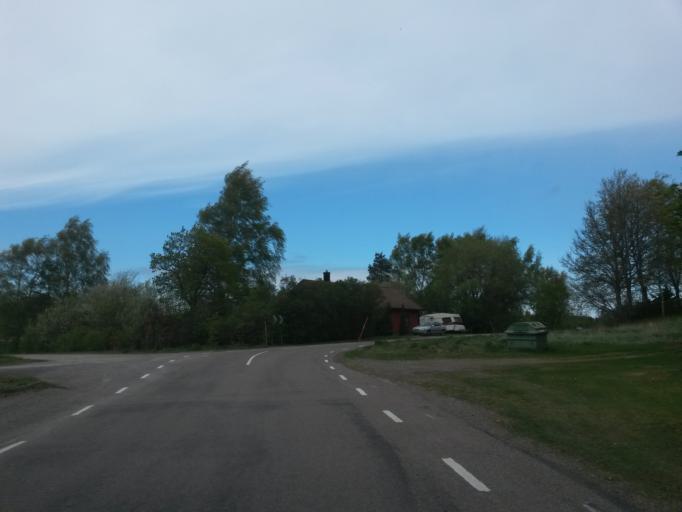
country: SE
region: Vaestra Goetaland
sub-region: Grastorps Kommun
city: Graestorp
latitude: 58.3948
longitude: 12.7937
